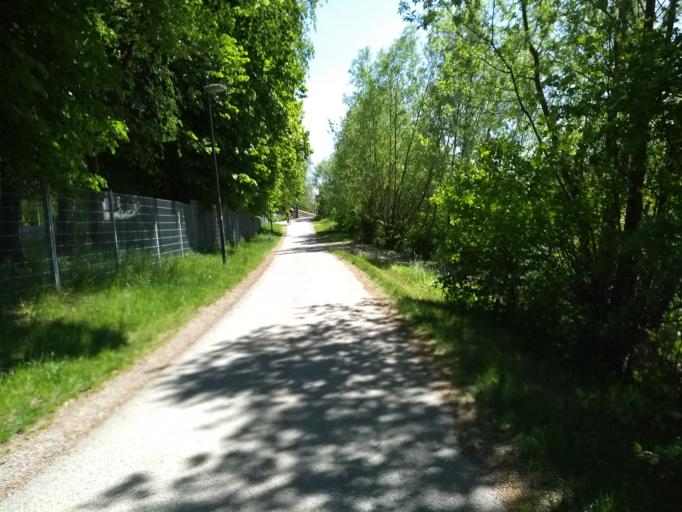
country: AT
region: Salzburg
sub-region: Politischer Bezirk Salzburg-Umgebung
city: Bergheim
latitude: 47.8271
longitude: 13.0317
